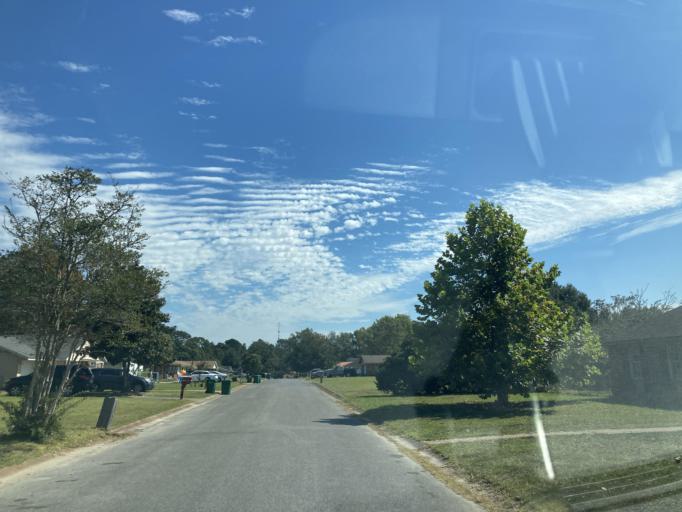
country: US
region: Mississippi
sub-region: Jackson County
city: Saint Martin
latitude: 30.4530
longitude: -88.8691
